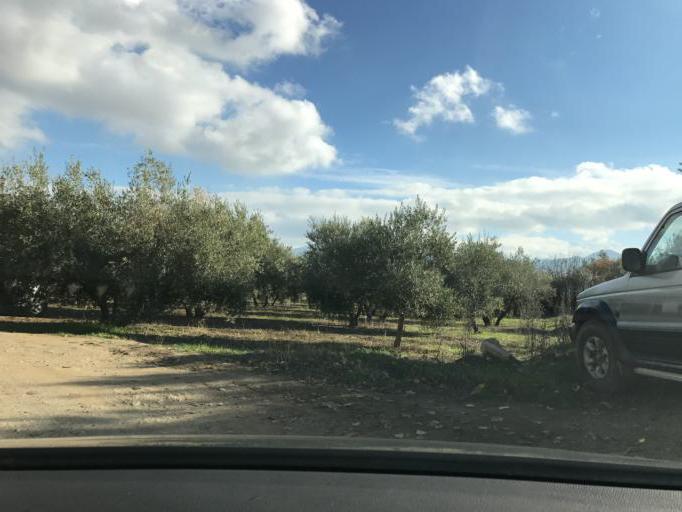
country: ES
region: Andalusia
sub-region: Provincia de Granada
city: Gojar
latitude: 37.1001
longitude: -3.6210
